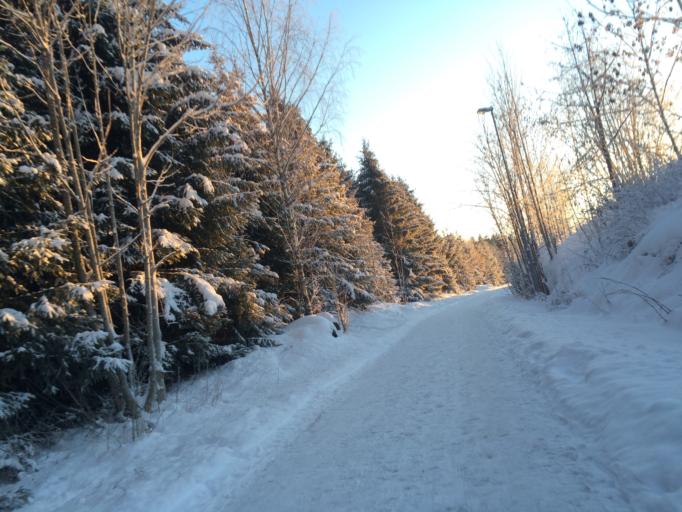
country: NO
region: Akershus
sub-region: Ski
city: Ski
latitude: 59.7059
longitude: 10.8346
